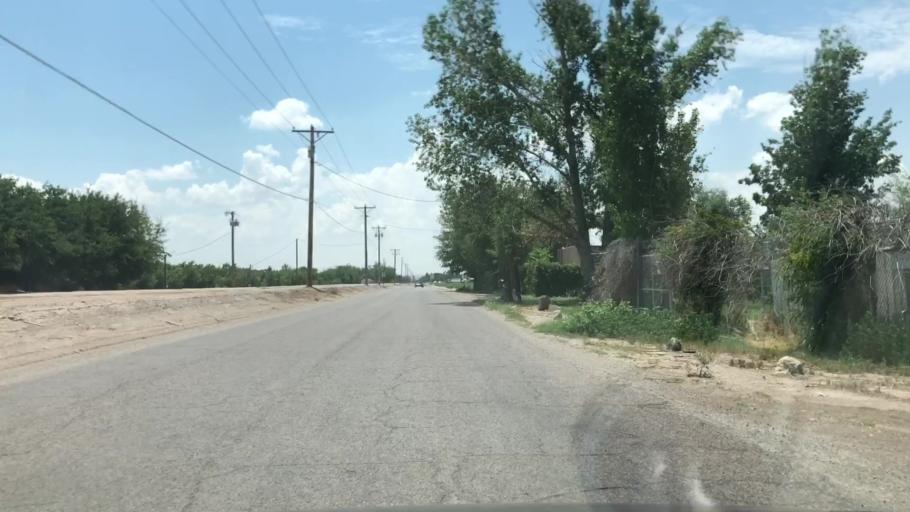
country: US
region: Texas
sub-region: El Paso County
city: Canutillo
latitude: 31.9142
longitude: -106.6249
